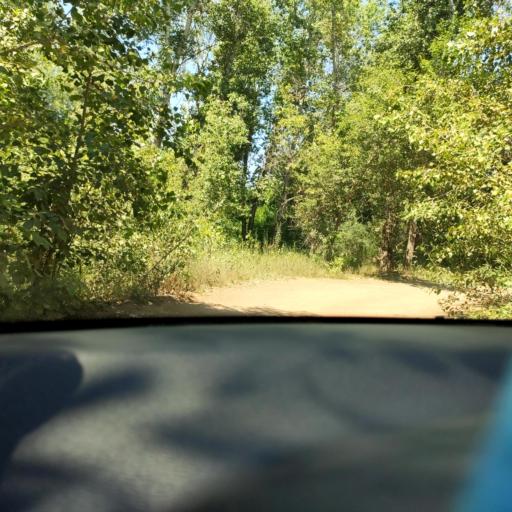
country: RU
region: Samara
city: Smyshlyayevka
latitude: 53.2214
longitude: 50.3435
